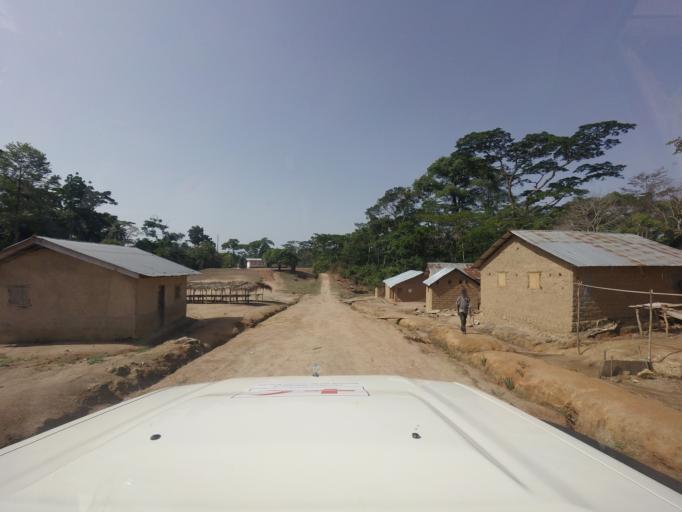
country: LR
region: Lofa
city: Voinjama
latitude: 8.5317
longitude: -9.7578
